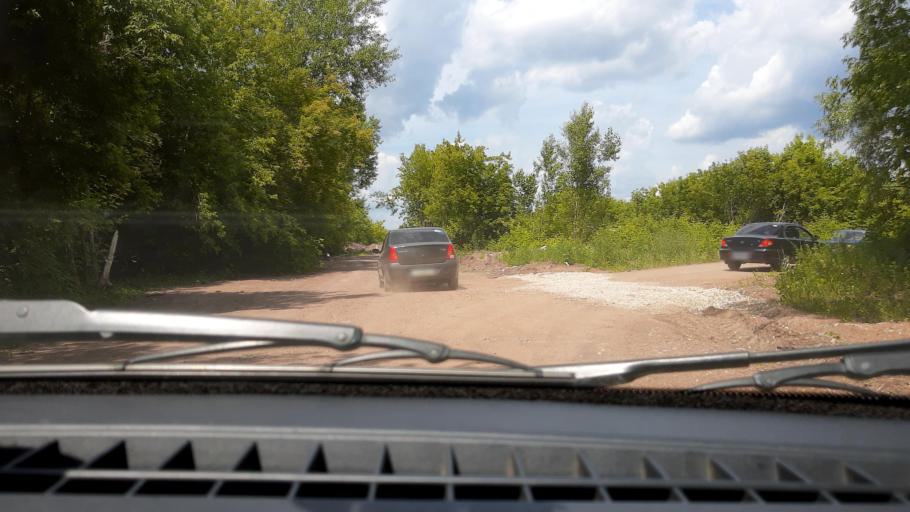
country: RU
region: Bashkortostan
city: Mikhaylovka
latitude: 54.7739
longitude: 55.9109
